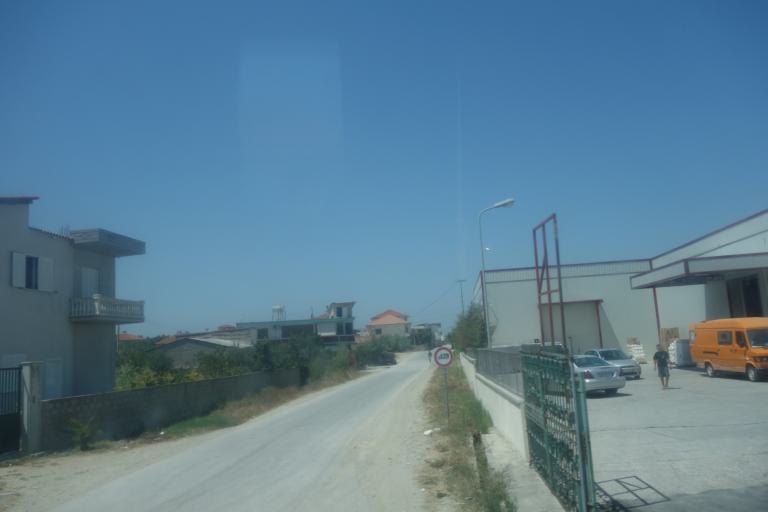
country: AL
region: Fier
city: Fier
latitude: 40.7083
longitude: 19.5450
